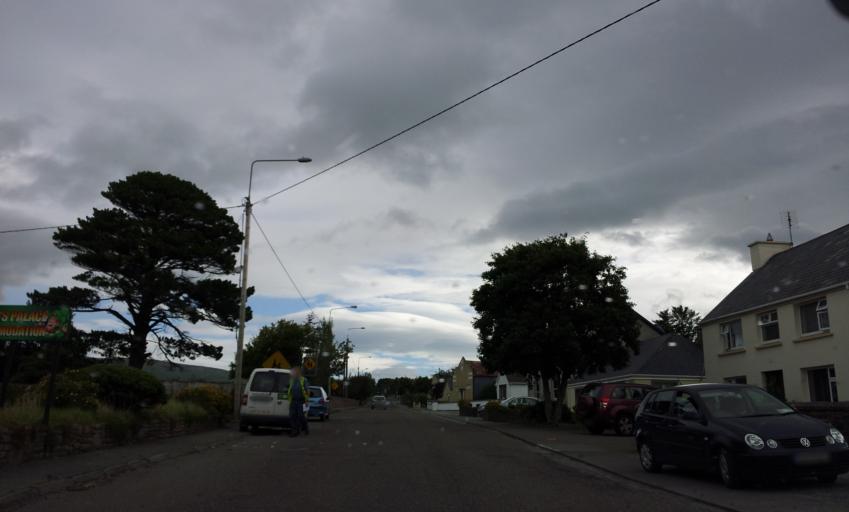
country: IE
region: Munster
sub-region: Ciarrai
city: Dingle
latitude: 52.1529
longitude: -10.0507
